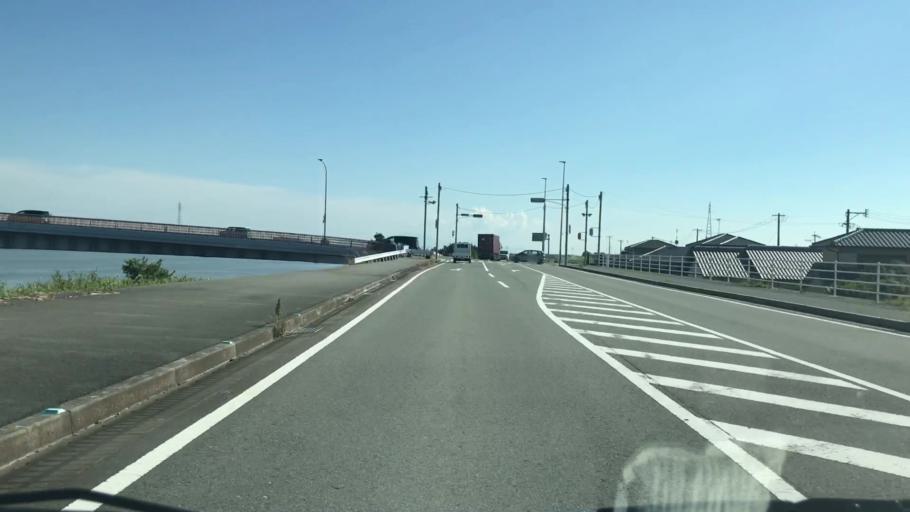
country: JP
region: Saga Prefecture
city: Okawa
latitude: 33.2371
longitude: 130.3803
